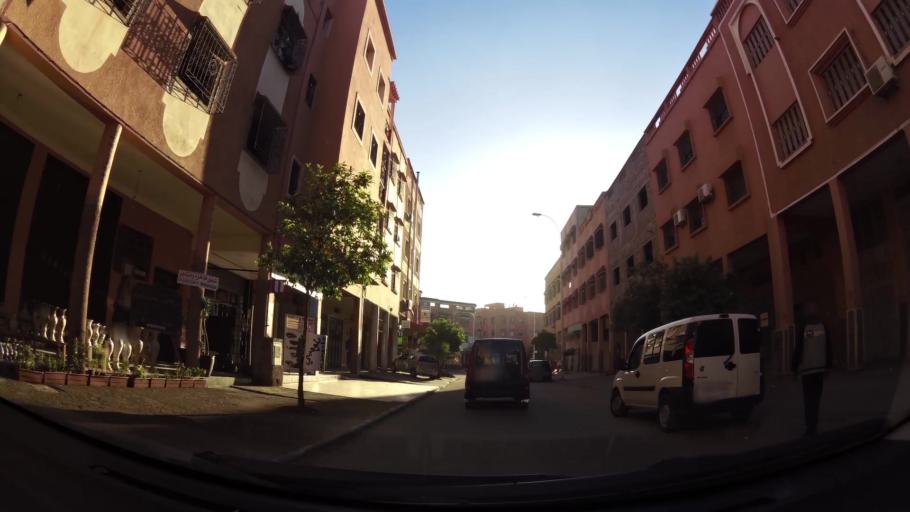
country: MA
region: Marrakech-Tensift-Al Haouz
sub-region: Marrakech
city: Marrakesh
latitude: 31.6192
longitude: -8.0599
